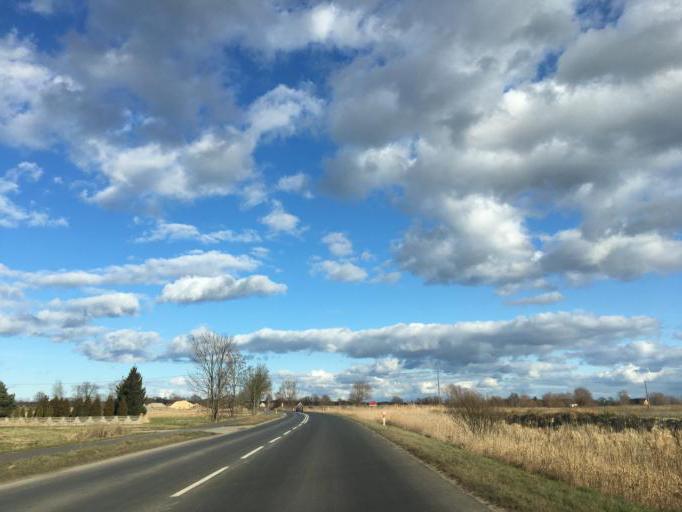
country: PL
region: Pomeranian Voivodeship
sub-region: Powiat gdanski
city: Cedry Wielkie
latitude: 54.3334
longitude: 18.8150
